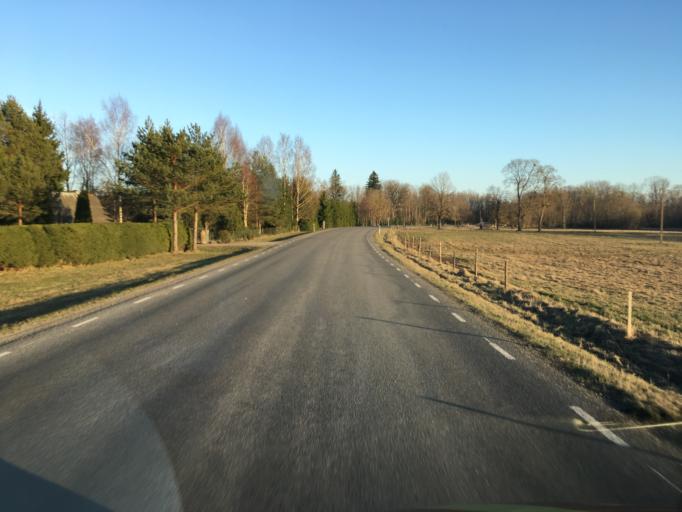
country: EE
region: Raplamaa
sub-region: Kehtna vald
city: Kehtna
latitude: 59.0264
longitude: 24.9257
